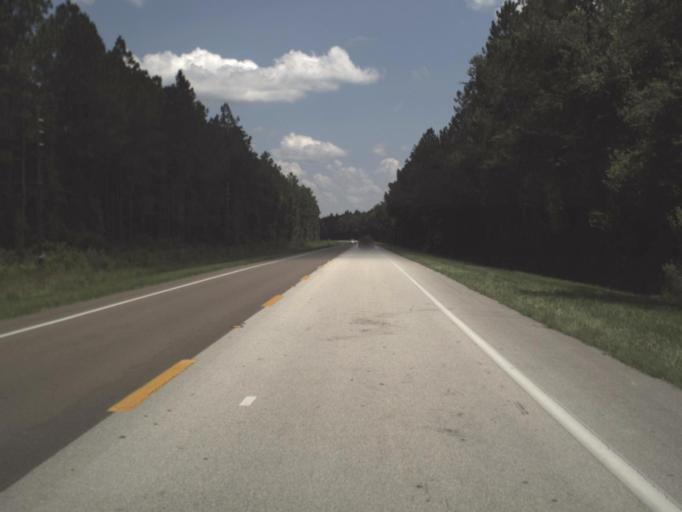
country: US
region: Florida
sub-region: Alachua County
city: Alachua
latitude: 29.7344
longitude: -82.3538
